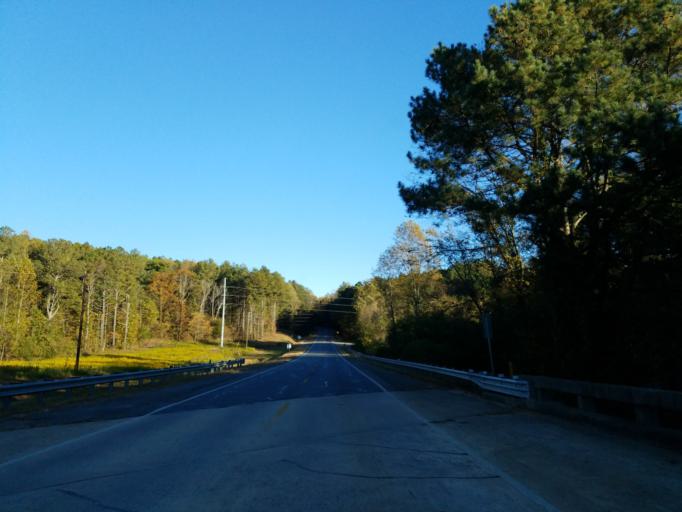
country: US
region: Georgia
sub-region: Dawson County
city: Dawsonville
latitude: 34.4208
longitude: -84.1464
